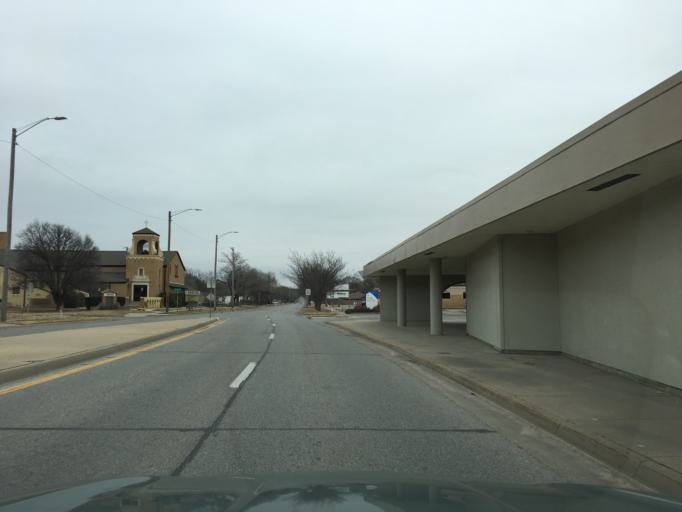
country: US
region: Kansas
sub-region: Sedgwick County
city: Wichita
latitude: 37.6718
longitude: -97.3071
